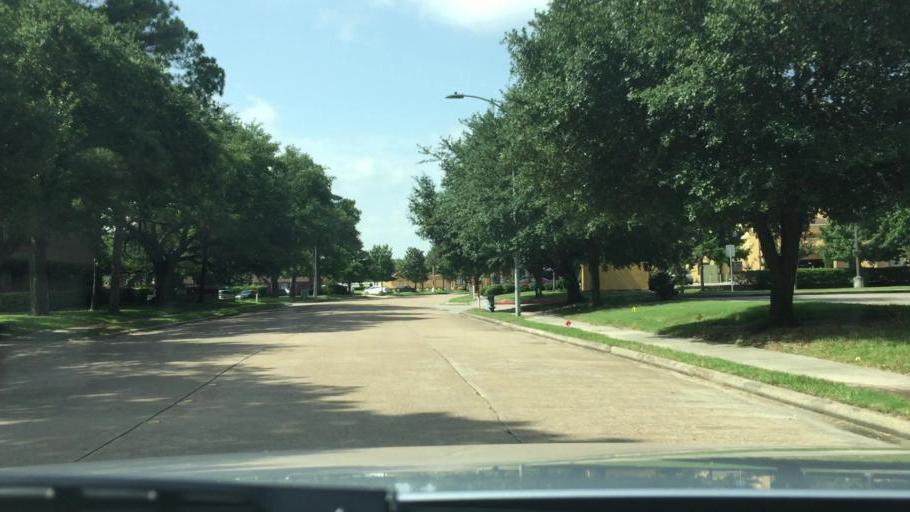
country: US
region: Texas
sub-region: Harris County
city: Hudson
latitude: 29.8460
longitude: -95.4949
